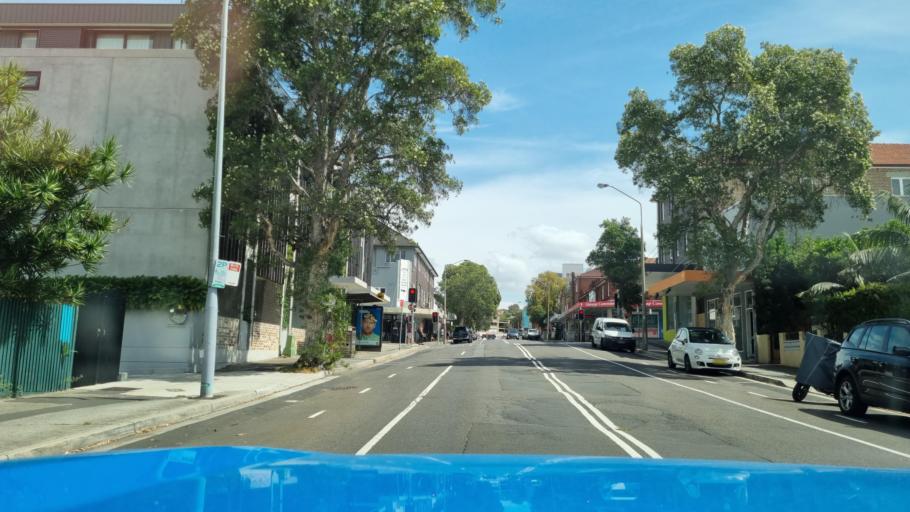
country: AU
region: New South Wales
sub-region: Waverley
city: North Bondi
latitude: -33.8869
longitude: 151.2724
